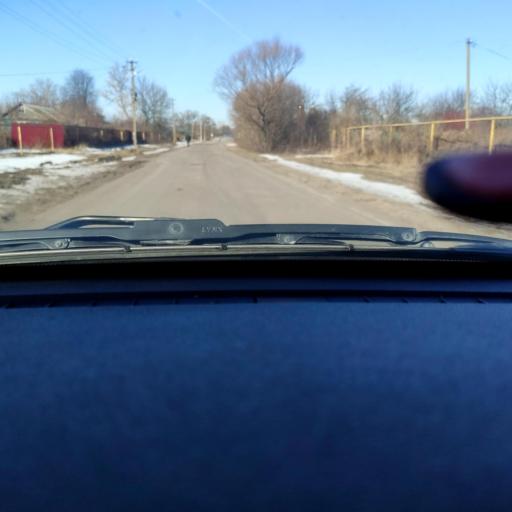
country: RU
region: Voronezj
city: Latnaya
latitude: 51.6973
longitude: 38.9363
